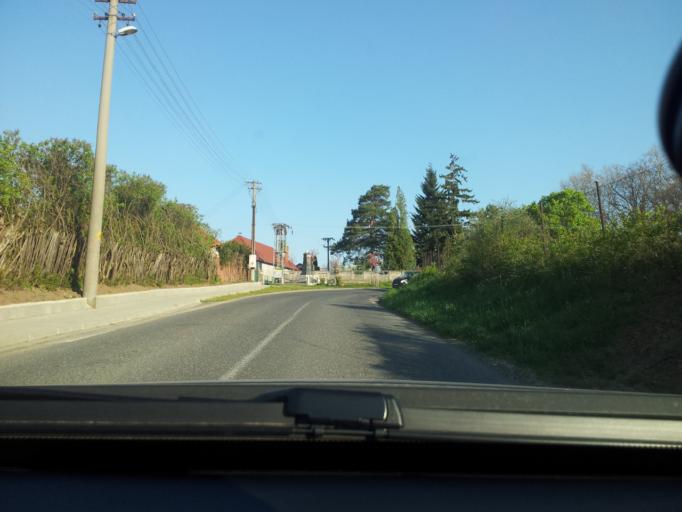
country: SK
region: Nitriansky
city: Tlmace
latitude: 48.3056
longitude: 18.4458
